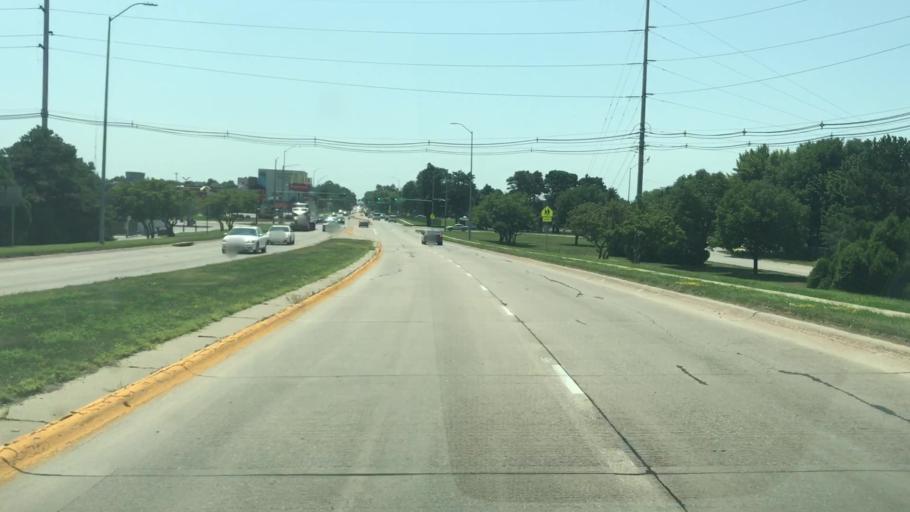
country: US
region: Nebraska
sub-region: Adams County
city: Hastings
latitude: 40.6039
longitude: -98.3921
